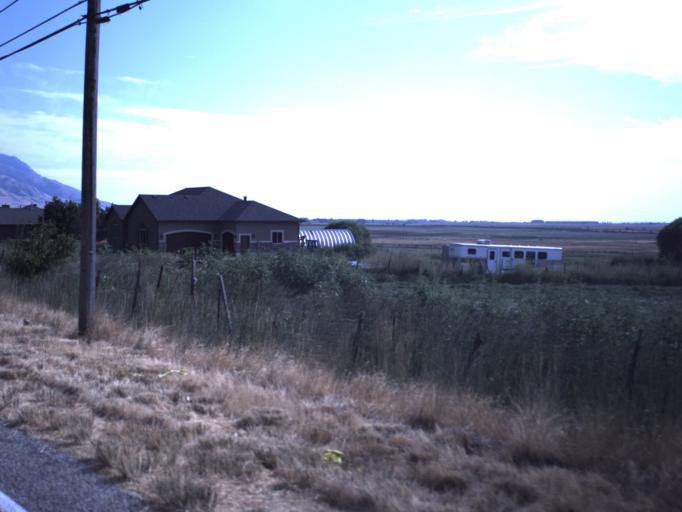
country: US
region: Utah
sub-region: Box Elder County
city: Brigham City
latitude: 41.5767
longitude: -112.0326
